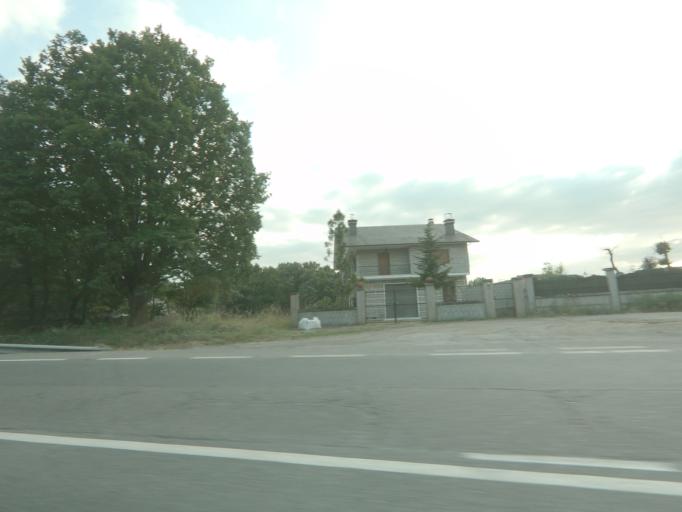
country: ES
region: Galicia
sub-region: Provincia de Ourense
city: Taboadela
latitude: 42.2670
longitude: -7.8366
